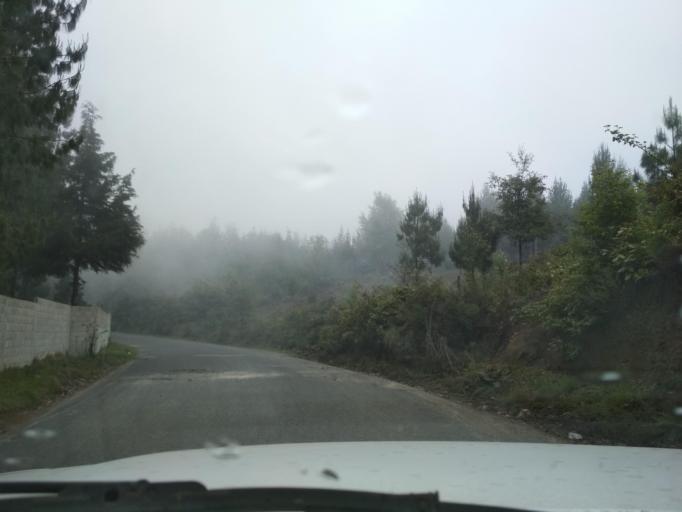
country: MX
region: Veracruz
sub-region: Mariano Escobedo
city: Loma Grande
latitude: 18.9331
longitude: -97.2202
